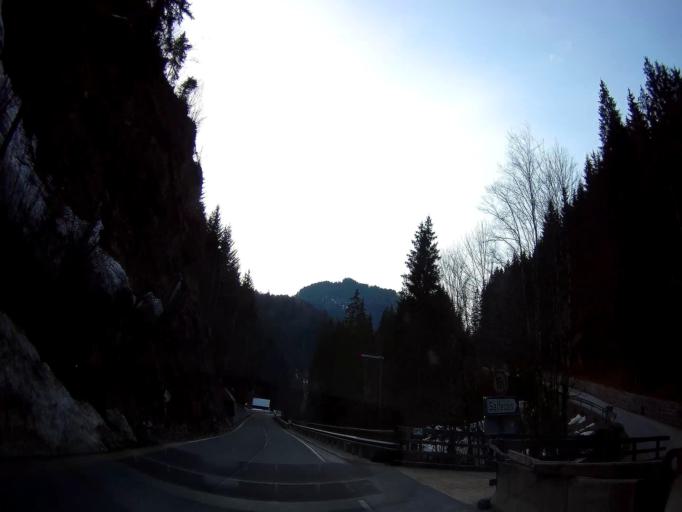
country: AT
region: Salzburg
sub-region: Politischer Bezirk Hallein
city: Abtenau
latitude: 47.5452
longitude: 13.4185
